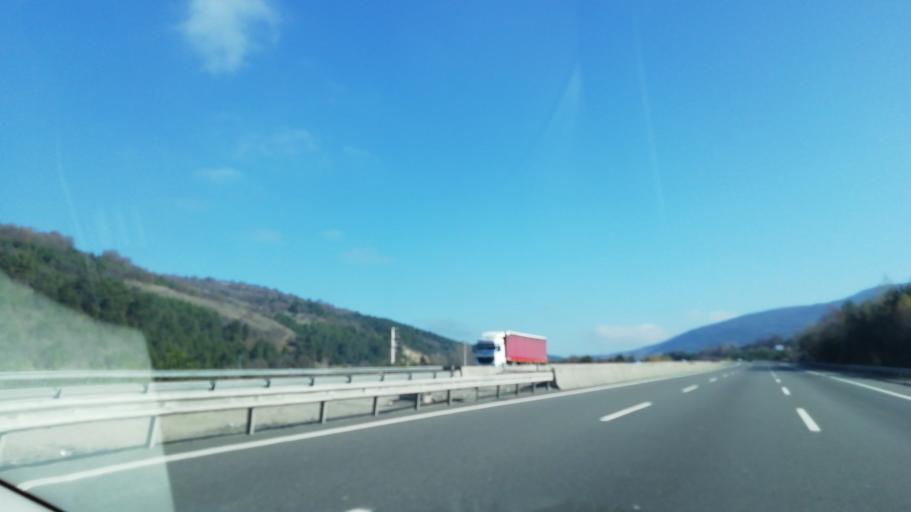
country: TR
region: Bolu
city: Gokcesu
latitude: 40.7393
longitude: 31.8293
